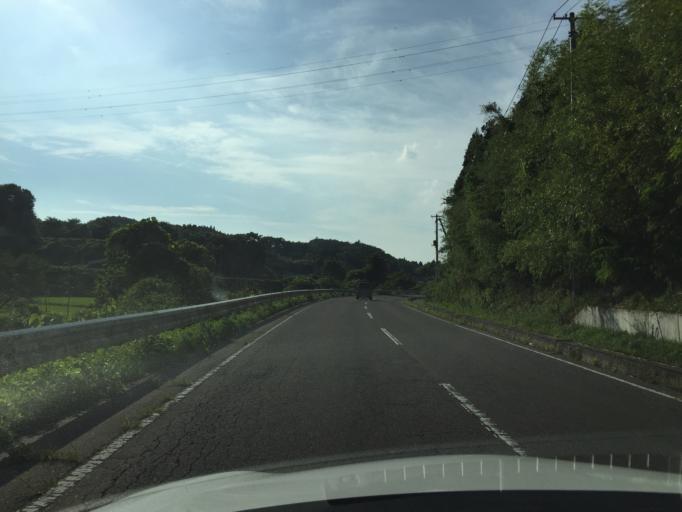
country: JP
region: Fukushima
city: Miharu
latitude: 37.3912
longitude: 140.5055
